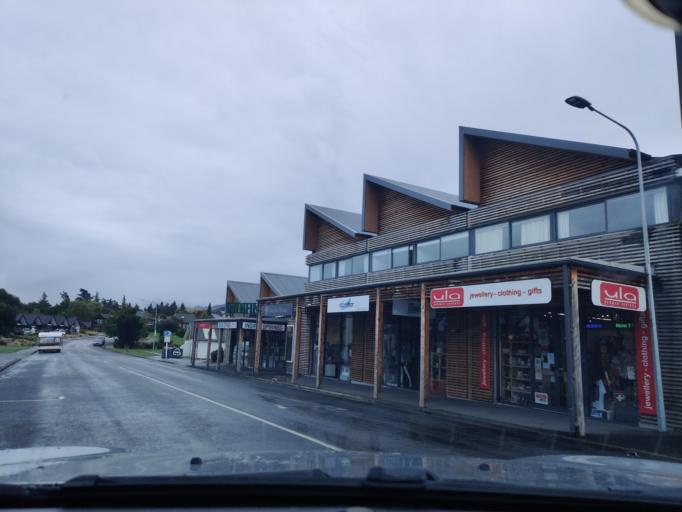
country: NZ
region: Canterbury
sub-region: Hurunui District
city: Amberley
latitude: -42.5199
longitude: 172.8293
